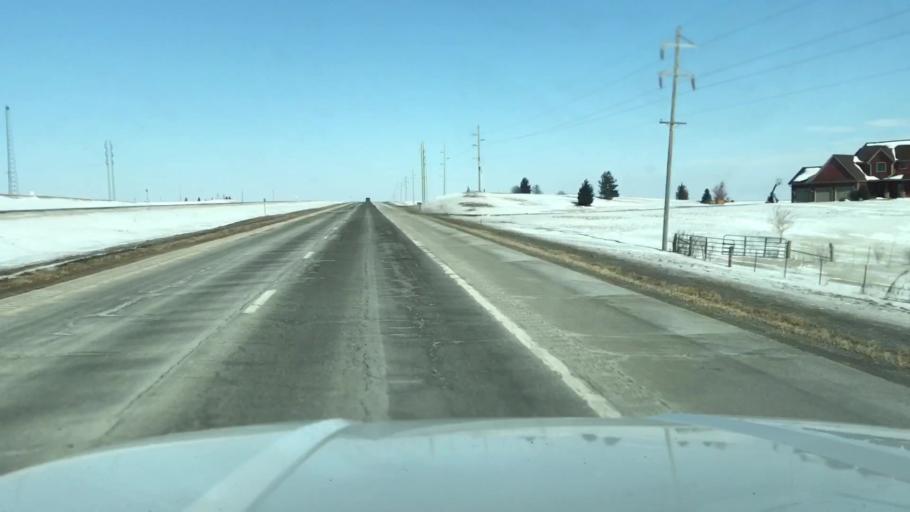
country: US
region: Missouri
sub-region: Nodaway County
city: Maryville
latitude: 40.2239
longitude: -94.8678
